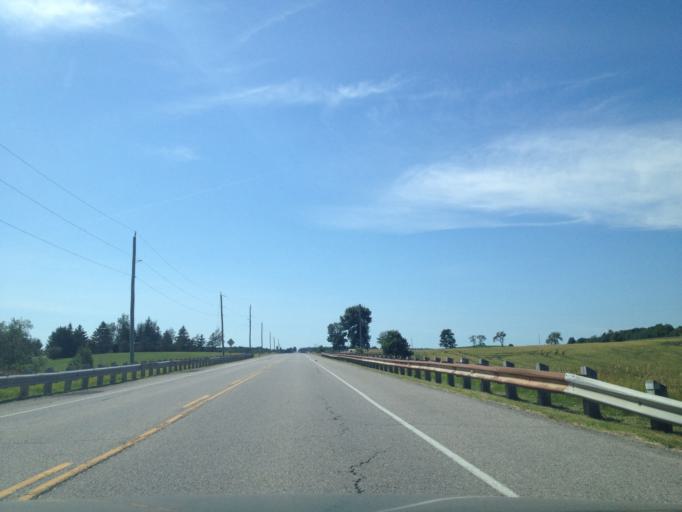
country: CA
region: Ontario
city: Stratford
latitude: 43.4793
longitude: -80.8232
